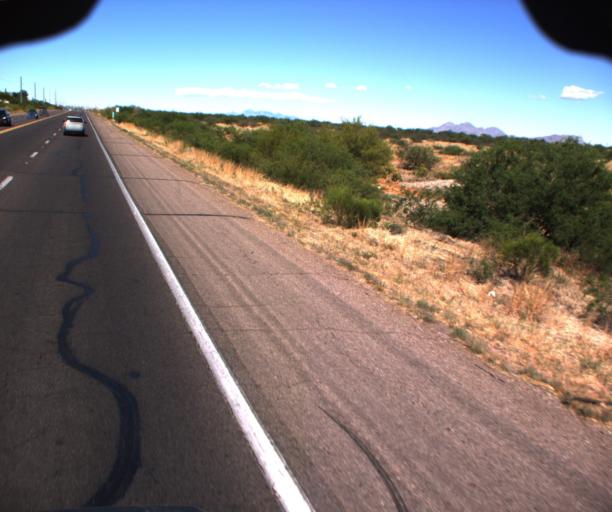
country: US
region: Arizona
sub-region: Cochise County
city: Sierra Vista
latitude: 31.5695
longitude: -110.2830
